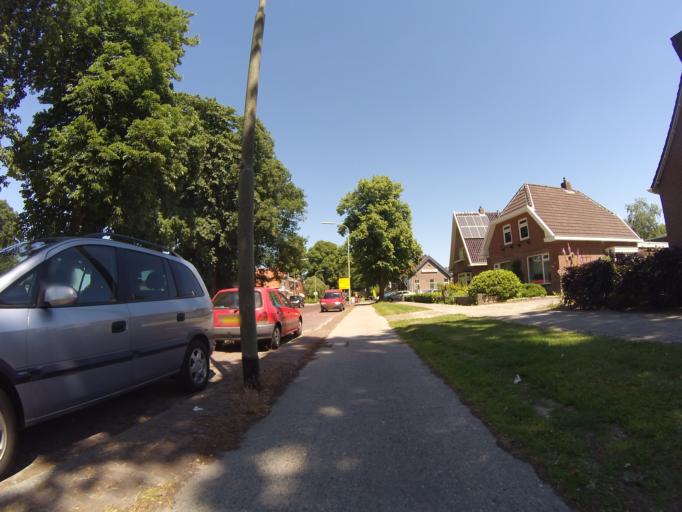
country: NL
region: Drenthe
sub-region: Gemeente Emmen
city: Emmen
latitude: 52.8183
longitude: 6.9167
